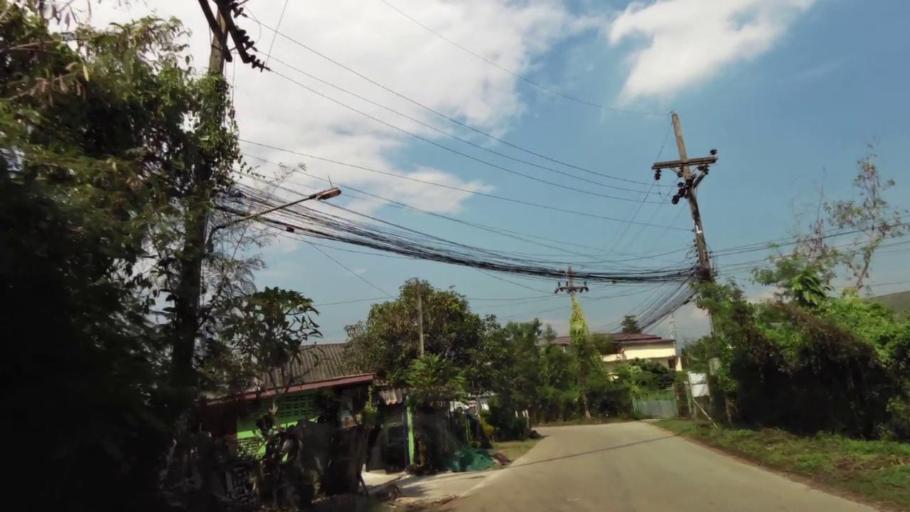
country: TH
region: Chiang Rai
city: Chiang Rai
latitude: 19.8888
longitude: 99.8029
